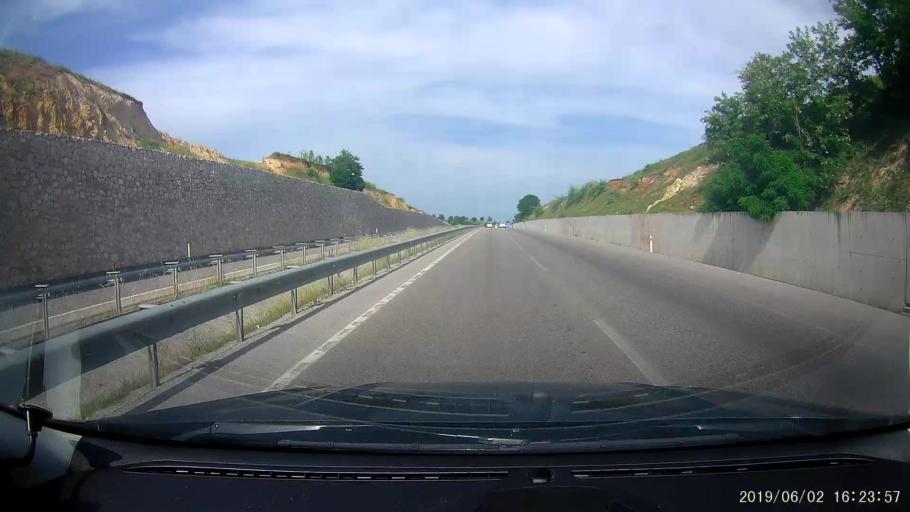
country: TR
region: Samsun
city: Havza
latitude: 40.9964
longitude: 35.7474
